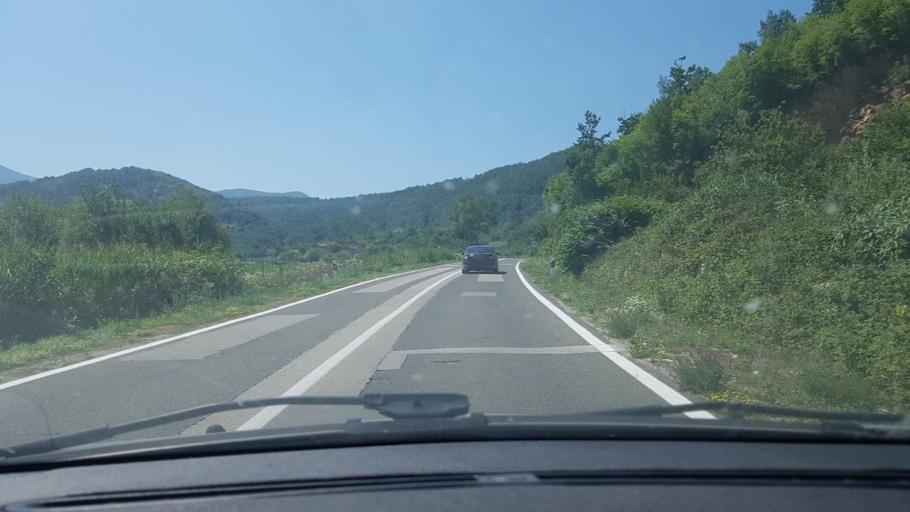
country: BA
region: Federation of Bosnia and Herzegovina
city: Bihac
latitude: 44.7510
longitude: 15.9368
